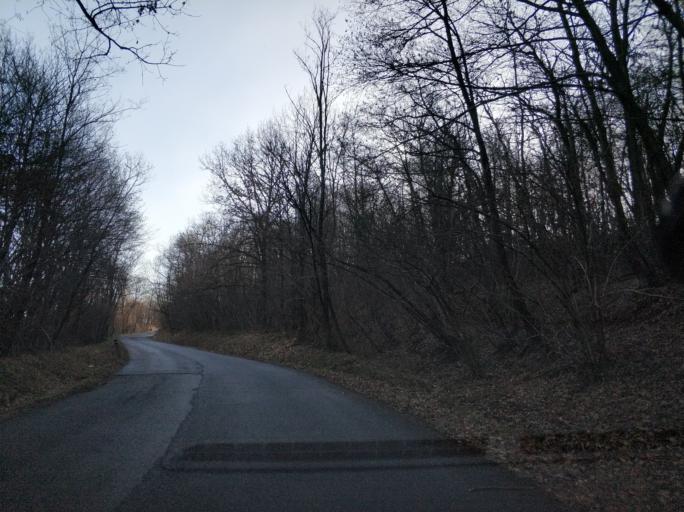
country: IT
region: Piedmont
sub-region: Provincia di Torino
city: Vauda Canavese Superiore
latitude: 45.2682
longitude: 7.6363
